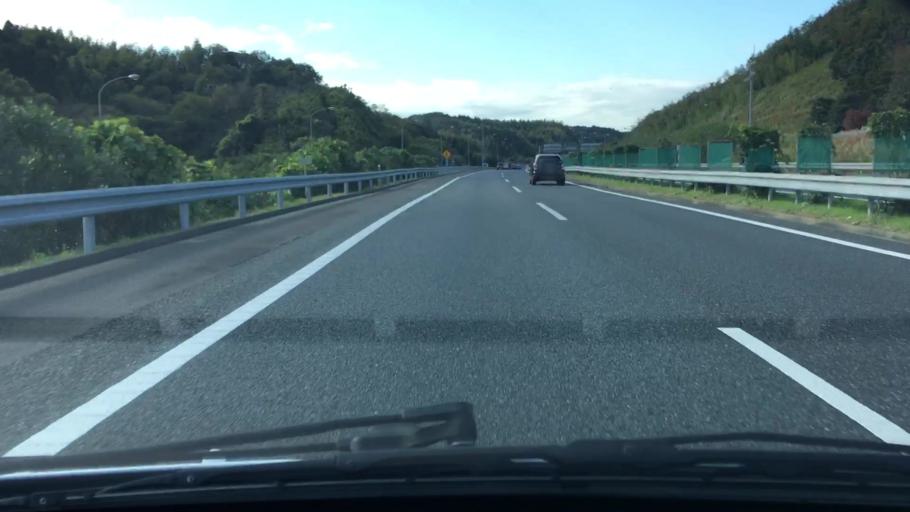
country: JP
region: Chiba
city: Kisarazu
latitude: 35.3743
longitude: 139.9774
